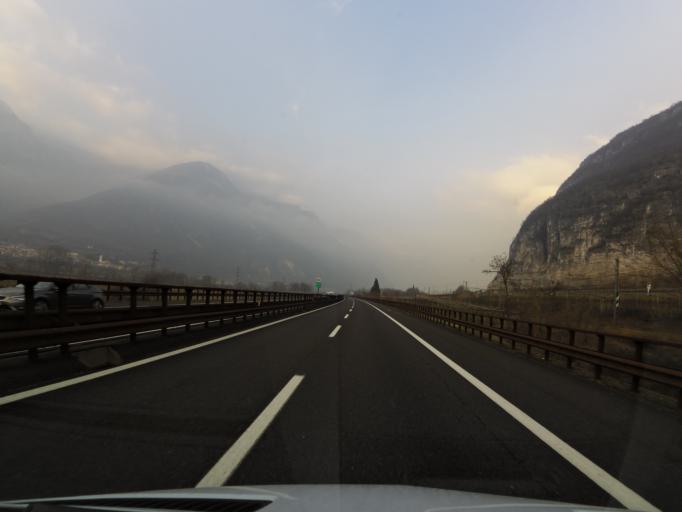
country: IT
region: Veneto
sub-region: Provincia di Verona
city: Rivalta
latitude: 45.6786
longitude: 10.9044
